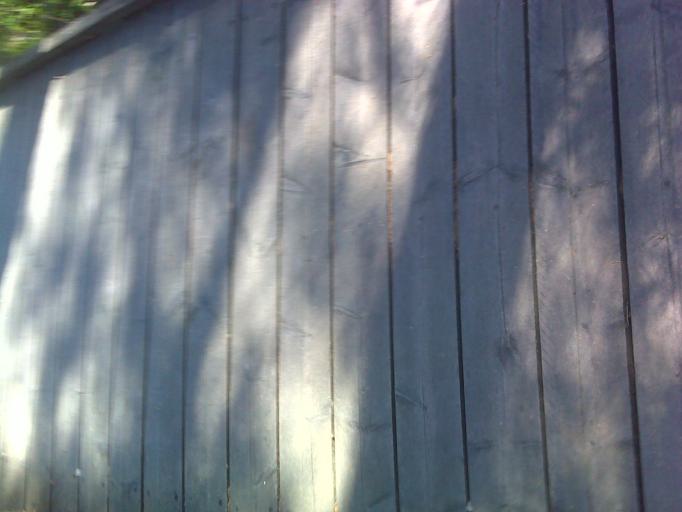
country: SE
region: Vaesternorrland
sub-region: OErnskoeldsviks Kommun
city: Kopmanholmen
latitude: 63.1342
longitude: 18.5169
